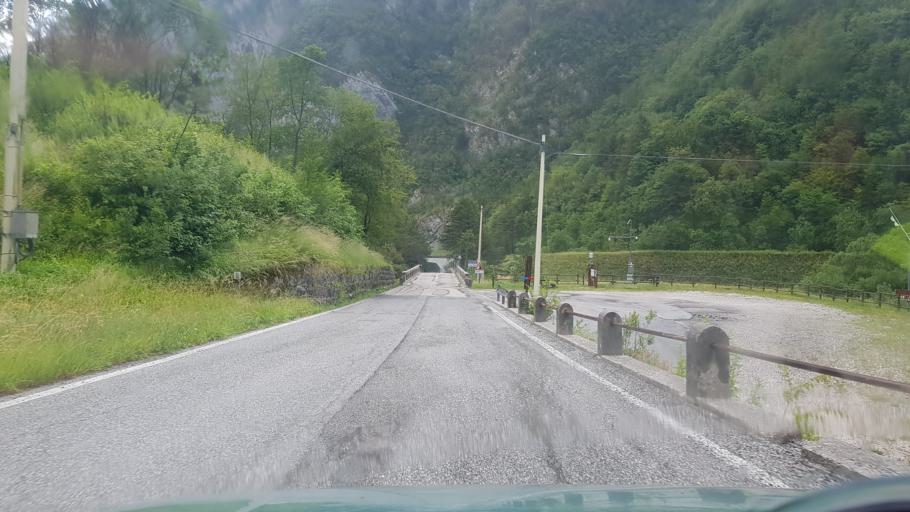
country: IT
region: Friuli Venezia Giulia
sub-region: Provincia di Udine
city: Lusevera
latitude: 46.3074
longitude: 13.2736
